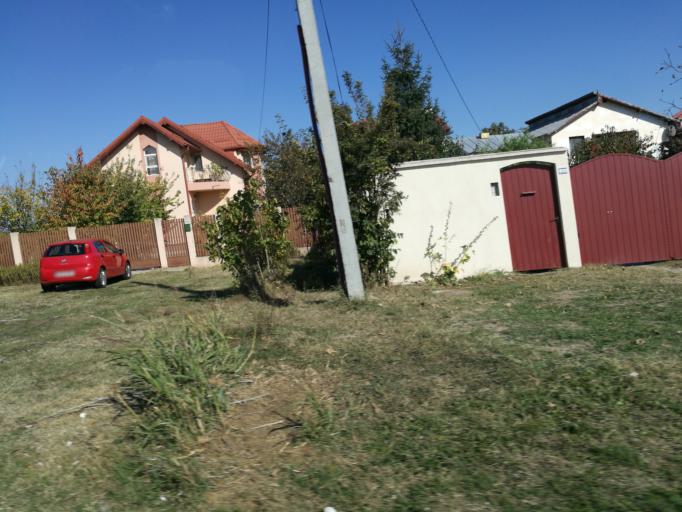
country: RO
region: Ilfov
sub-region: Comuna Dragomiresti-Vale
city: Dragomiresti-Vale
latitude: 44.4676
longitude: 25.9238
